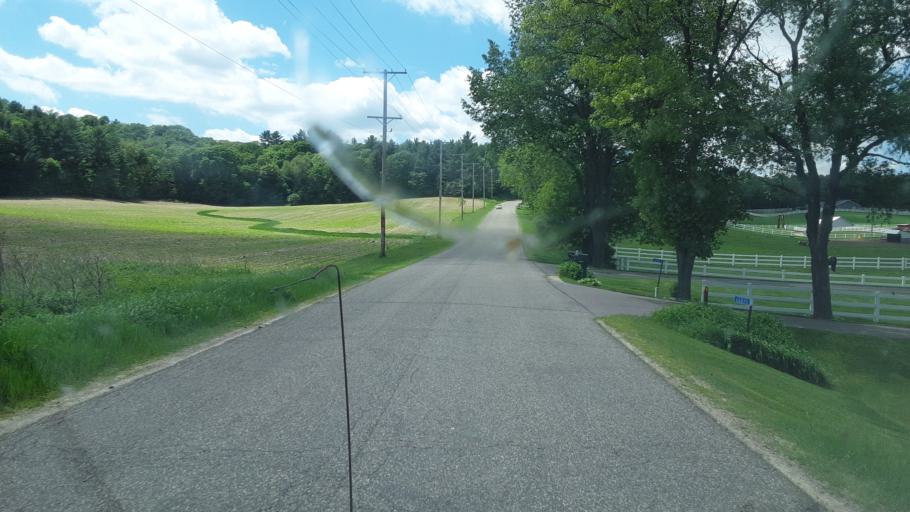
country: US
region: Wisconsin
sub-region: Sauk County
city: Reedsburg
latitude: 43.5623
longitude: -89.9792
